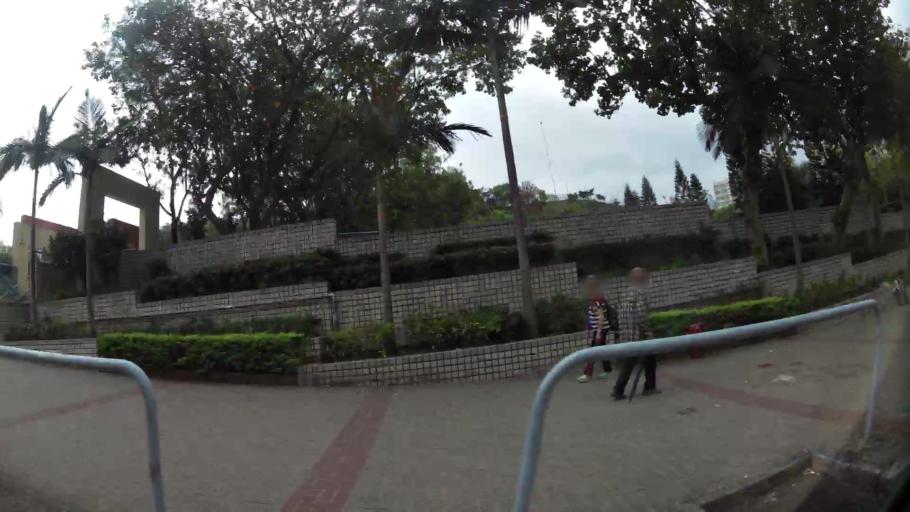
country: HK
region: Kowloon City
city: Kowloon
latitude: 22.3195
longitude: 114.2234
